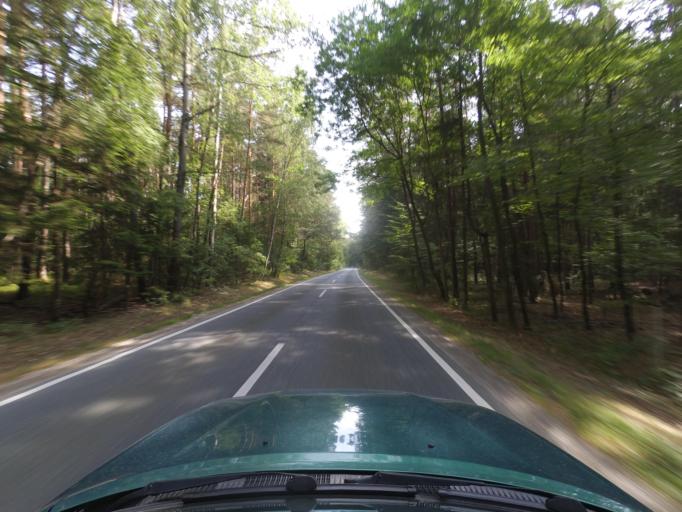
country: DE
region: Bavaria
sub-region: Regierungsbezirk Mittelfranken
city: Wieseth
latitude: 49.2079
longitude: 10.4510
